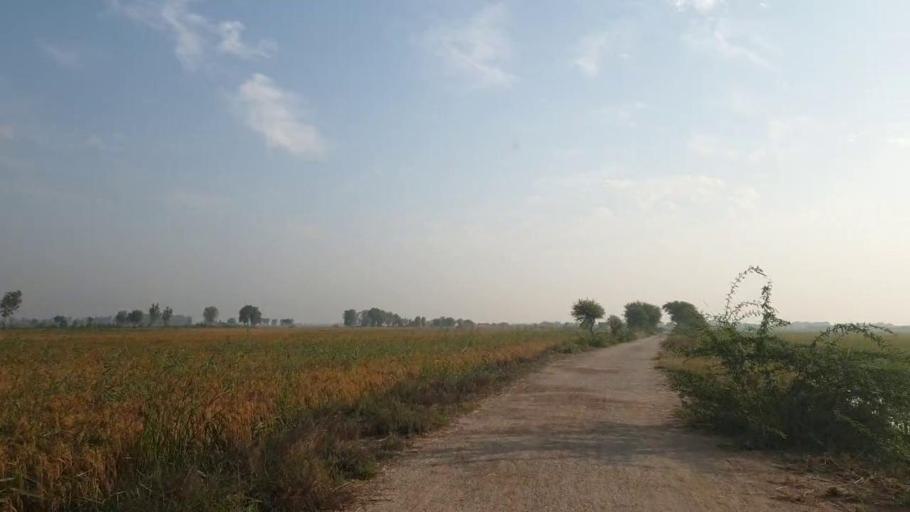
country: PK
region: Sindh
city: Tando Bago
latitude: 24.8174
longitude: 68.9540
